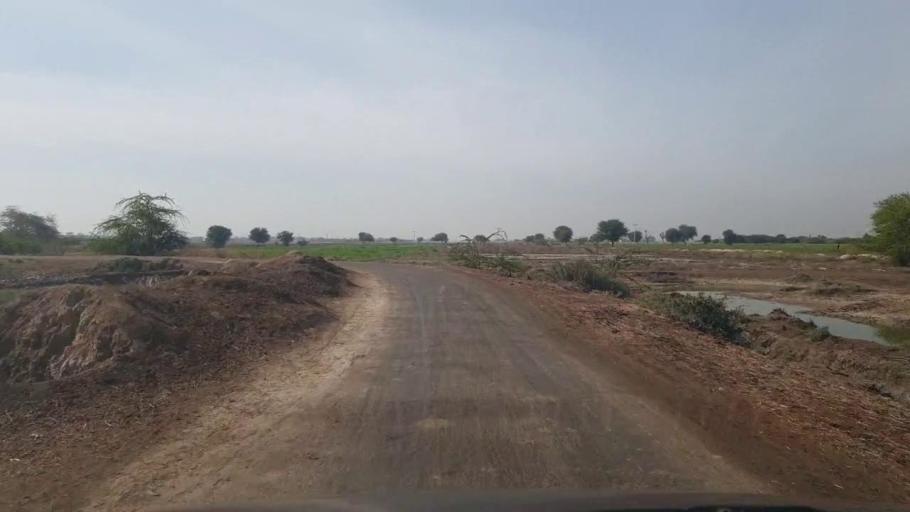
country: PK
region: Sindh
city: Umarkot
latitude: 25.3589
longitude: 69.6806
